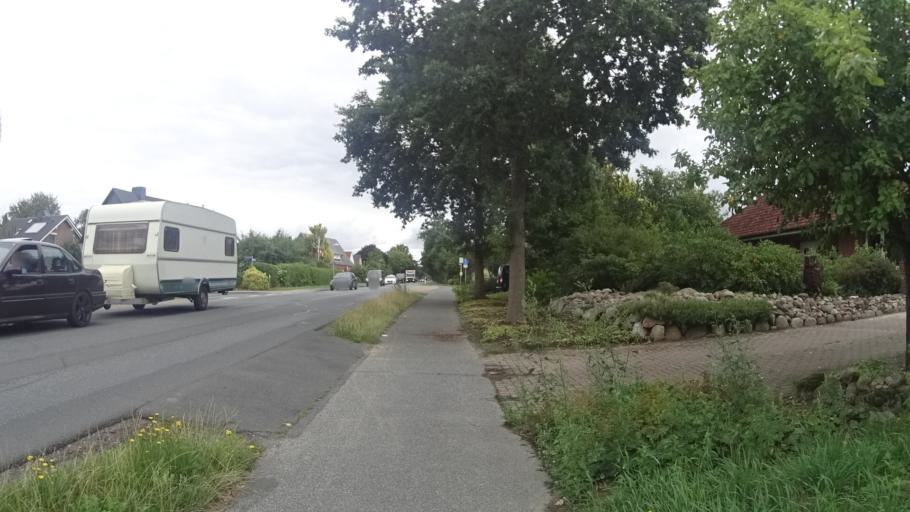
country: DE
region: Lower Saxony
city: Schiffdorf
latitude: 53.5483
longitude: 8.6909
